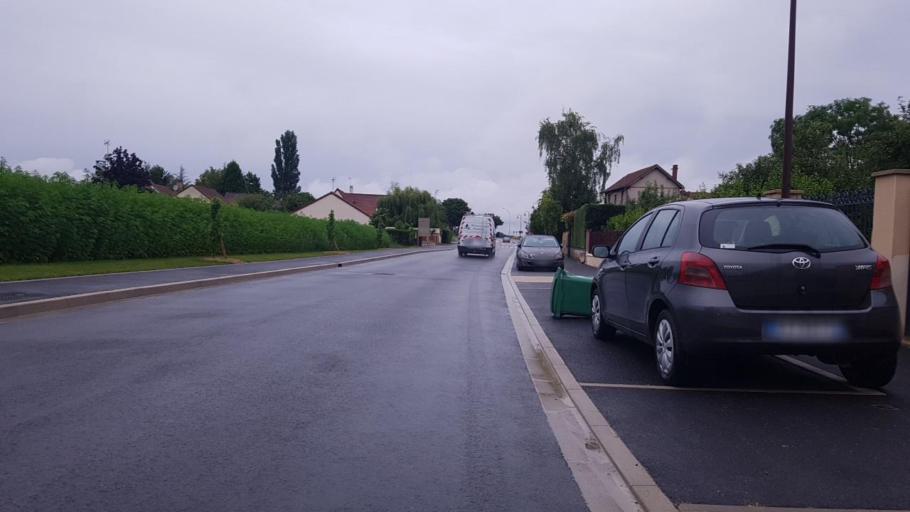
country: FR
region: Champagne-Ardenne
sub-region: Departement de la Marne
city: Sarry
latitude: 48.9216
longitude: 4.4010
